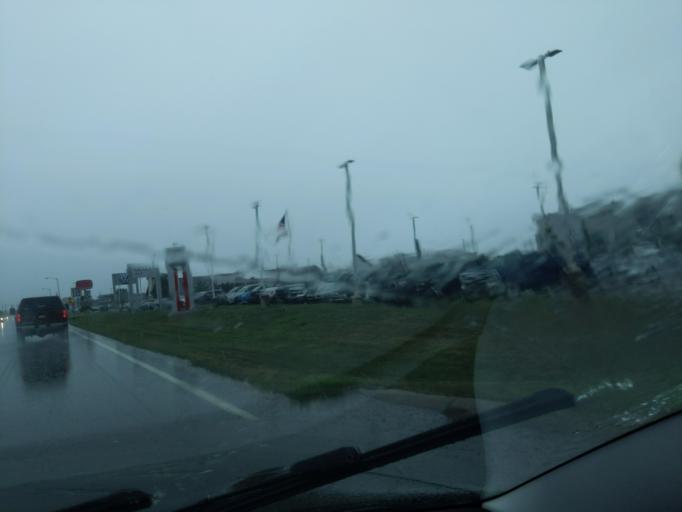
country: US
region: Michigan
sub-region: Muskegon County
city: Fruitport
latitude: 43.1542
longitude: -86.1985
